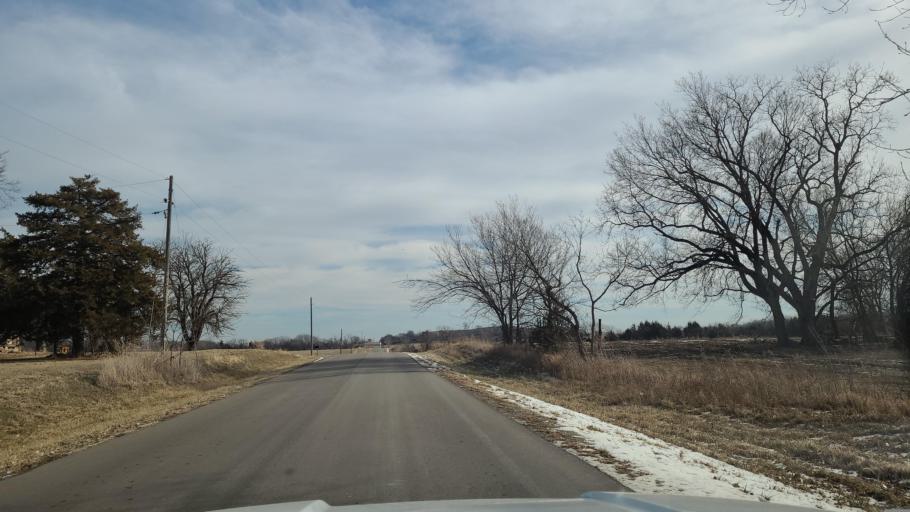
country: US
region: Kansas
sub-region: Douglas County
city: Lawrence
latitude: 38.8991
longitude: -95.1936
